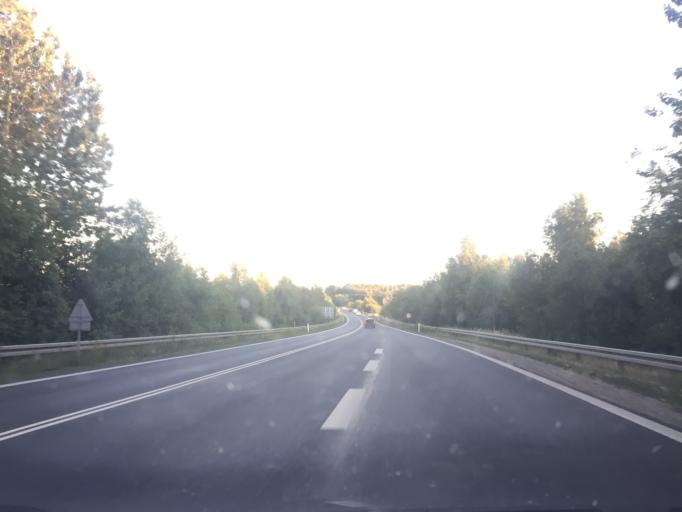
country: DK
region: Capital Region
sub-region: Gribskov Kommune
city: Helsinge
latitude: 56.0052
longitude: 12.2391
